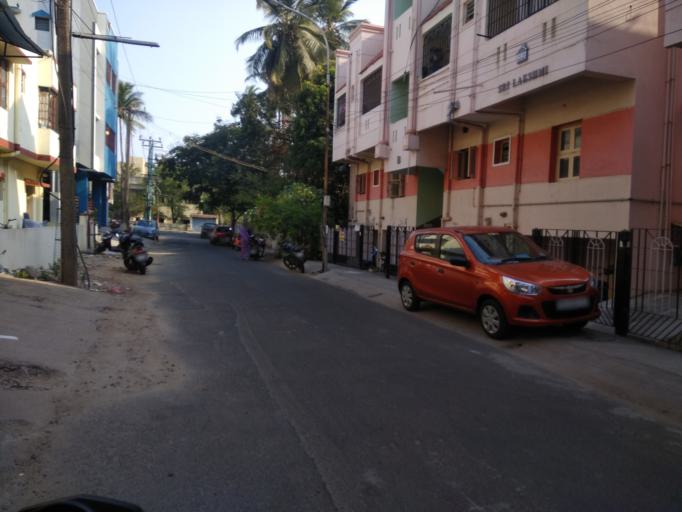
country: IN
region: Tamil Nadu
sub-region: Kancheepuram
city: Saint Thomas Mount
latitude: 12.9835
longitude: 80.1894
